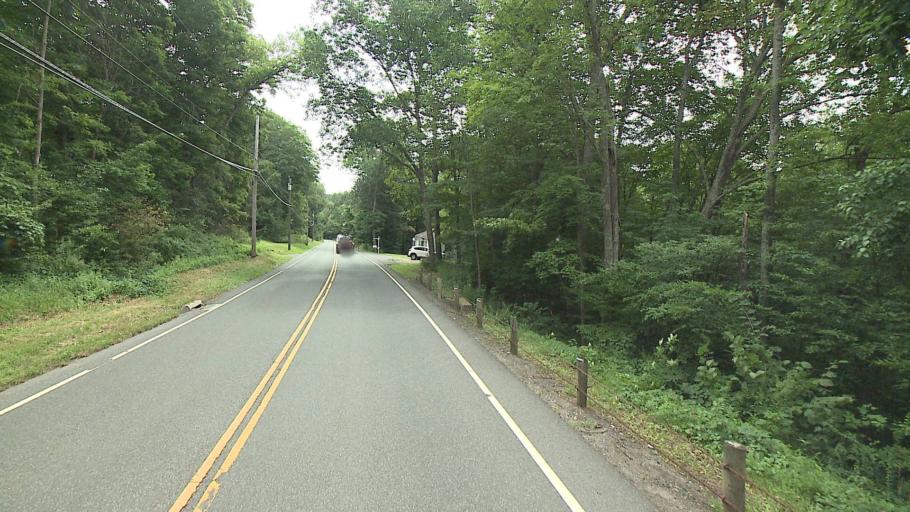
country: US
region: Connecticut
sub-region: Litchfield County
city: Woodbury
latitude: 41.5719
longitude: -73.2322
